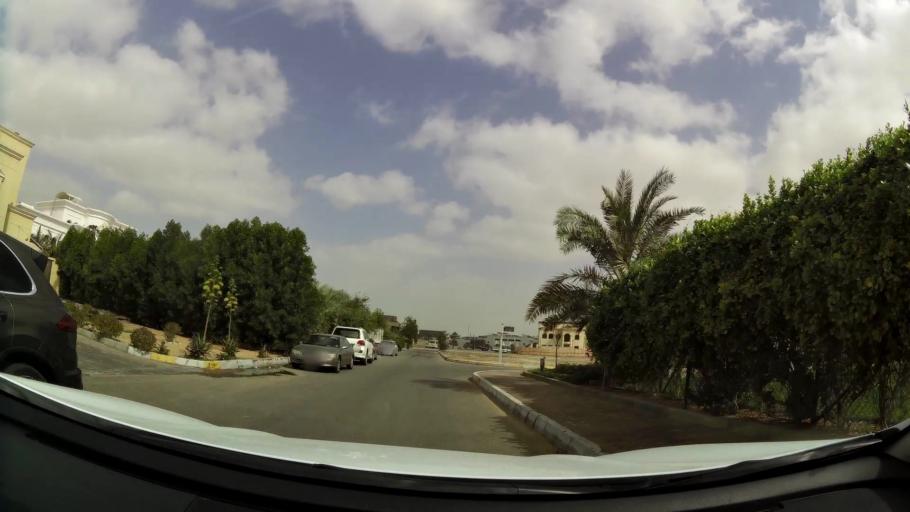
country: AE
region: Abu Dhabi
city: Abu Dhabi
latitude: 24.4132
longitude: 54.4938
